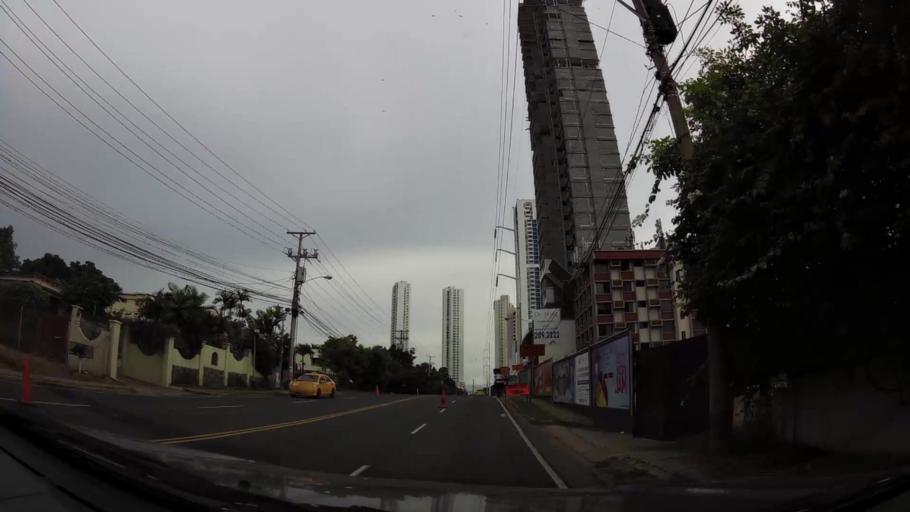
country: PA
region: Panama
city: Panama
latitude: 8.9999
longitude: -79.4972
